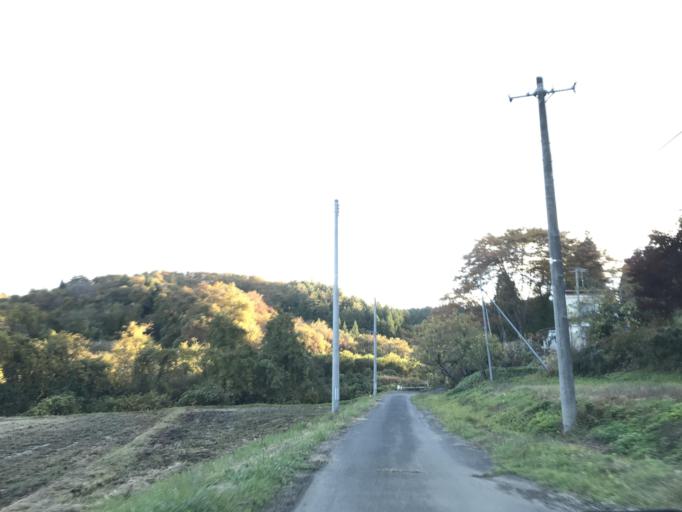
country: JP
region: Iwate
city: Ichinoseki
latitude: 38.8876
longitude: 141.1122
